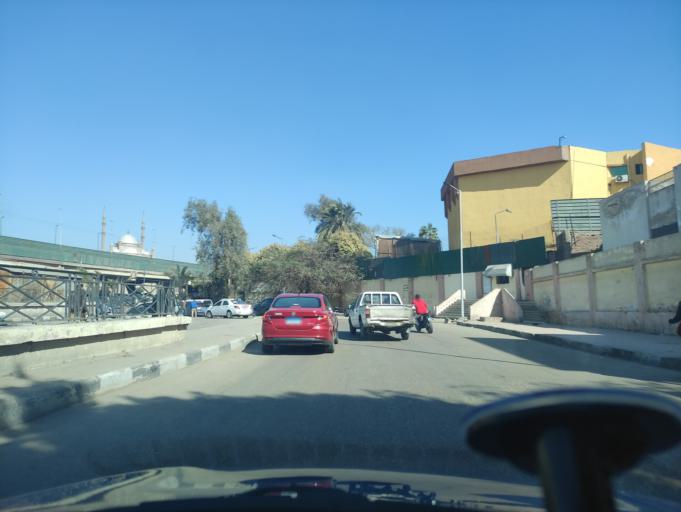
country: EG
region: Muhafazat al Qahirah
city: Cairo
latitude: 30.0241
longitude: 31.2636
